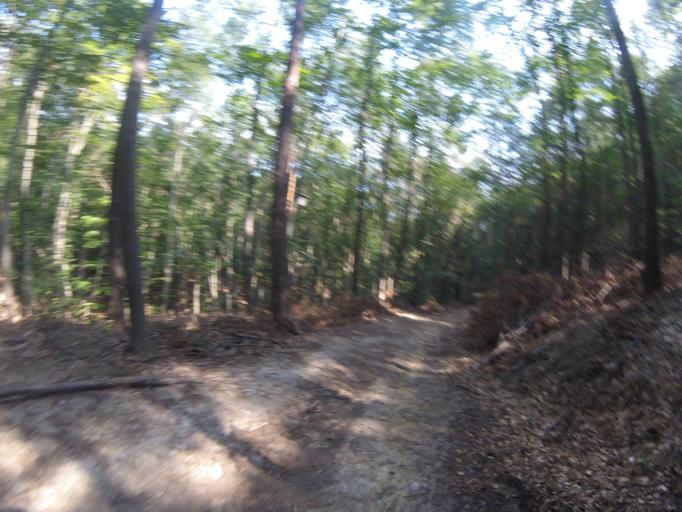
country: HU
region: Borsod-Abauj-Zemplen
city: Satoraljaujhely
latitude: 48.4507
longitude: 21.5744
